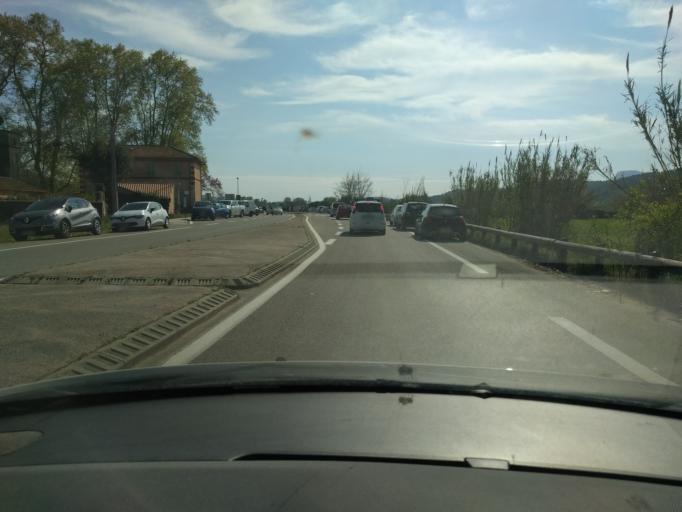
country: FR
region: Provence-Alpes-Cote d'Azur
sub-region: Departement du Var
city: Pierrefeu-du-Var
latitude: 43.1913
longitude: 6.1247
